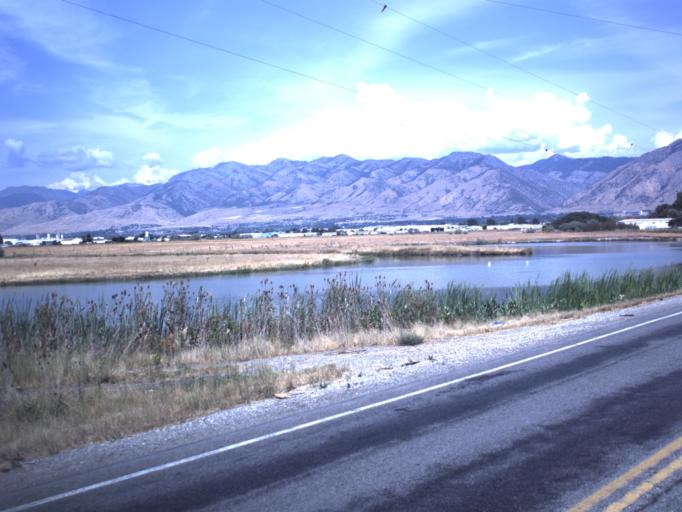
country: US
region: Utah
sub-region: Cache County
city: Logan
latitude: 41.7359
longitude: -111.8765
